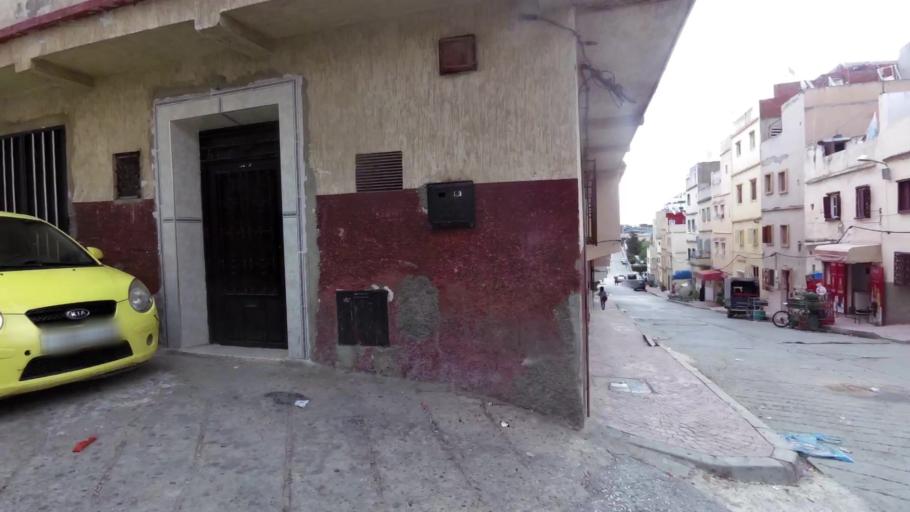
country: MA
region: Tanger-Tetouan
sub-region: Tanger-Assilah
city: Tangier
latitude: 35.7615
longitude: -5.8250
